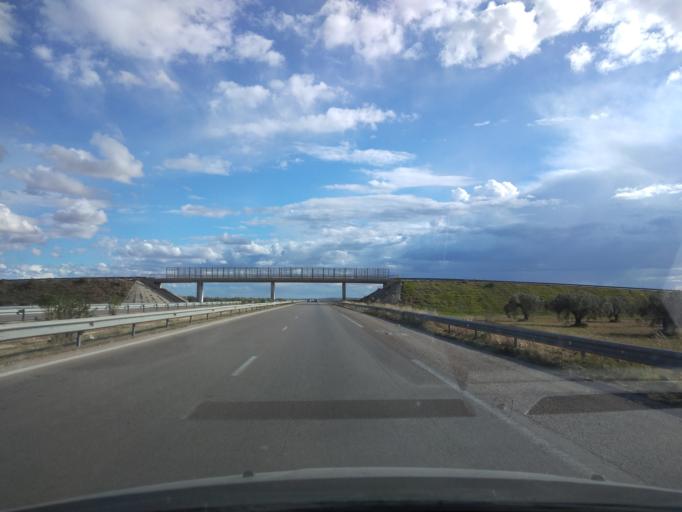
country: TN
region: Al Munastir
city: Manzil Kamil
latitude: 35.6195
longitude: 10.5946
